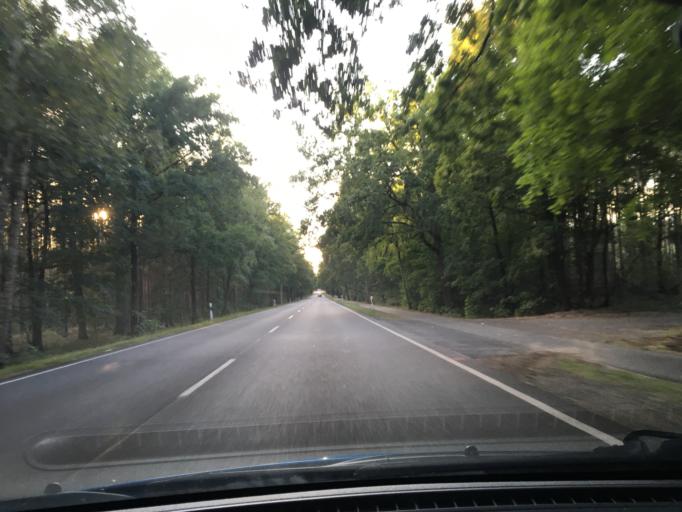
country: DE
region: Lower Saxony
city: Hambuhren
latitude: 52.6727
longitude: 10.0268
